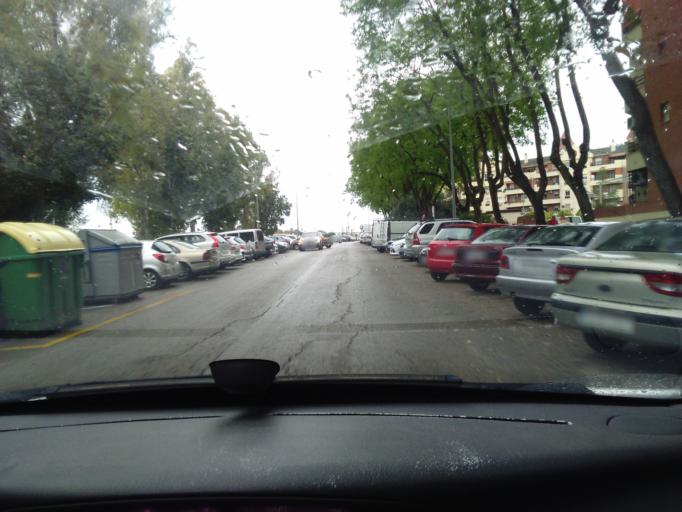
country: ES
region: Andalusia
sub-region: Provincia de Sevilla
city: Sevilla
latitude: 37.4026
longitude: -5.9365
